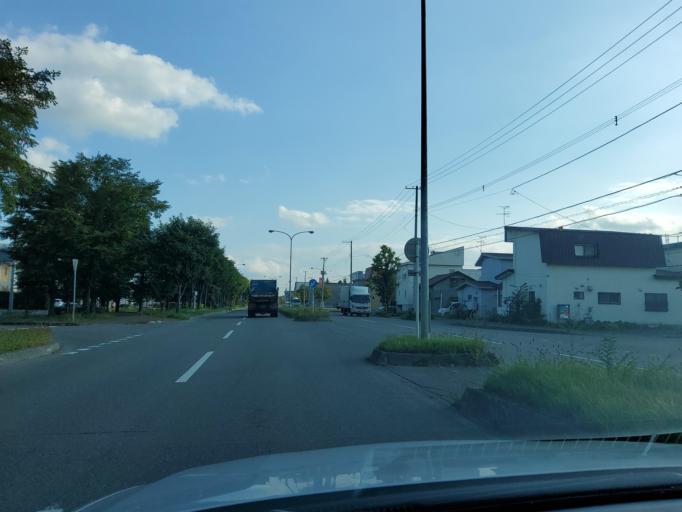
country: JP
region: Hokkaido
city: Obihiro
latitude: 42.9071
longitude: 143.2138
